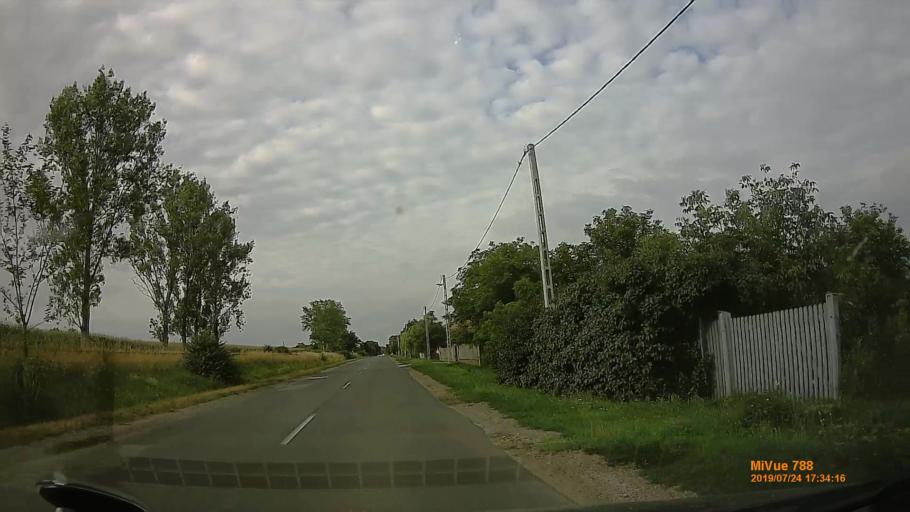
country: HU
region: Borsod-Abauj-Zemplen
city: Abaujszanto
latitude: 48.3025
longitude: 21.1969
